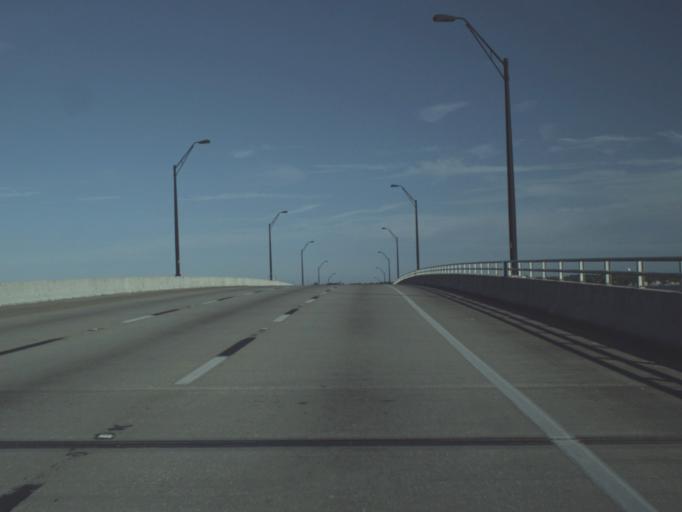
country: US
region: Florida
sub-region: Lee County
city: North Fort Myers
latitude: 26.6516
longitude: -81.8657
